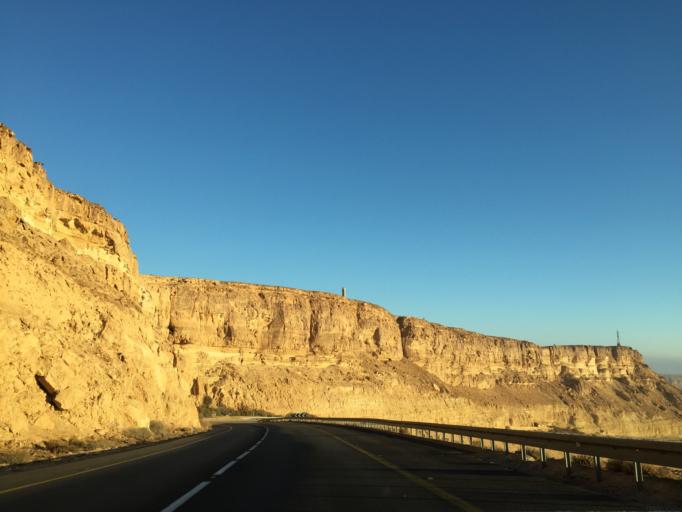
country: IL
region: Southern District
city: Mitzpe Ramon
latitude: 30.6147
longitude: 34.8091
